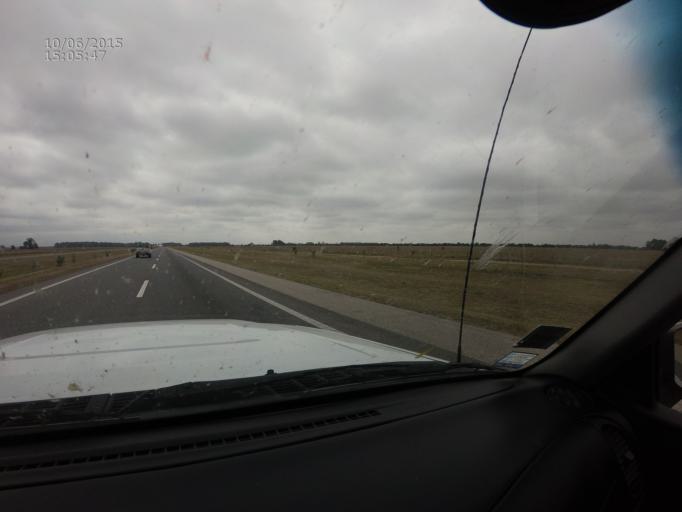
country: AR
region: Cordoba
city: Pilar
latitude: -31.6930
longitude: -63.8281
